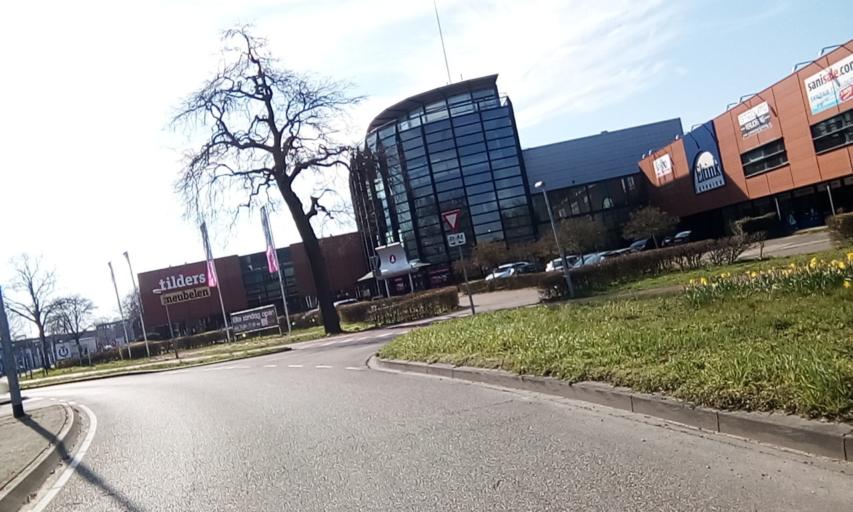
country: NL
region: Gelderland
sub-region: Gemeente Nijmegen
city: Lindenholt
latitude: 51.8180
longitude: 5.7672
